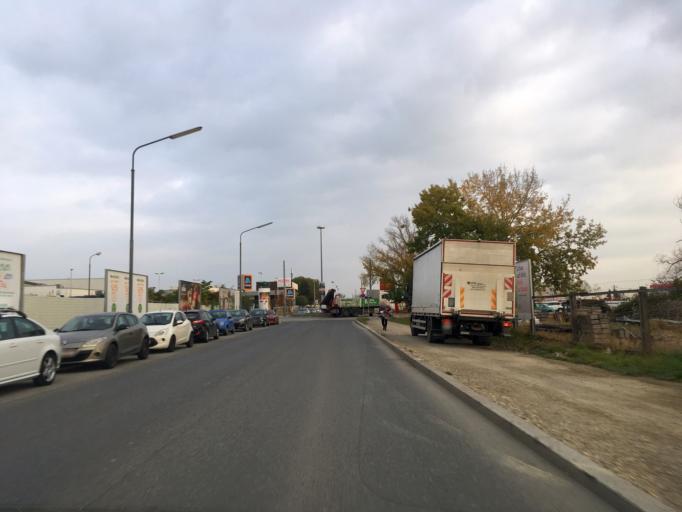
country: AT
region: Lower Austria
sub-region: Politischer Bezirk Wien-Umgebung
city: Gerasdorf bei Wien
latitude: 48.2530
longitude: 16.4604
